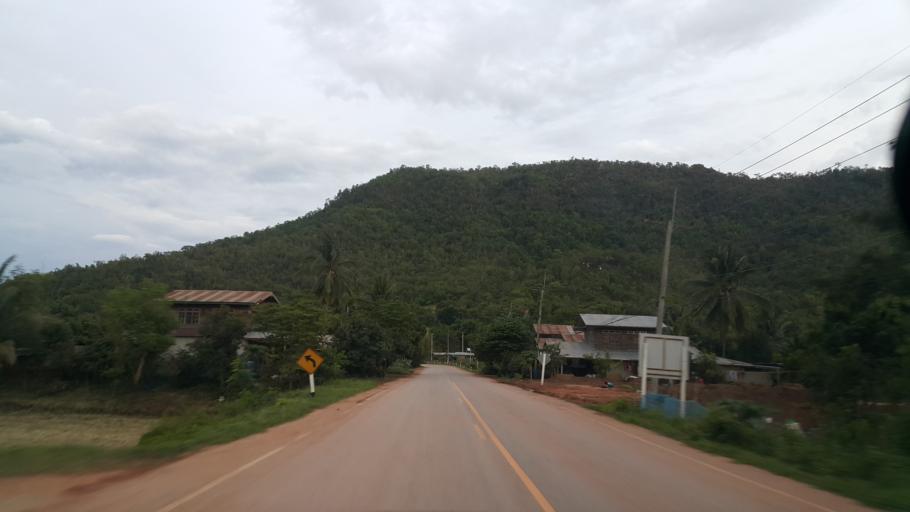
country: TH
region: Loei
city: Na Haeo
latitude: 17.5251
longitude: 101.1800
